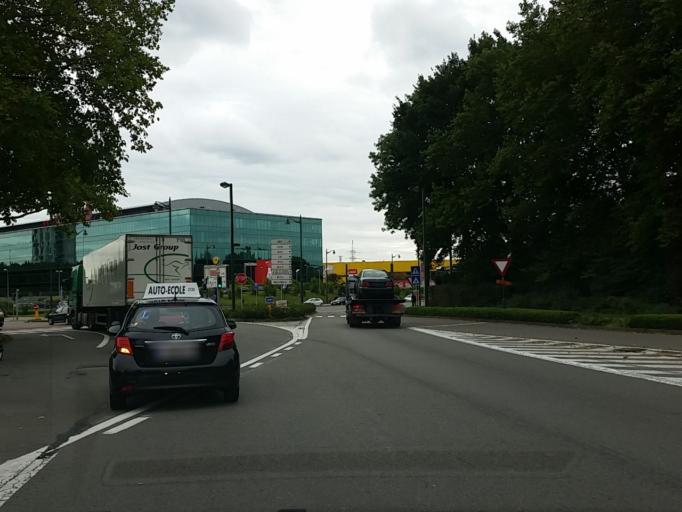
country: BE
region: Flanders
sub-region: Provincie Vlaams-Brabant
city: Drogenbos
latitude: 50.8139
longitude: 4.2886
